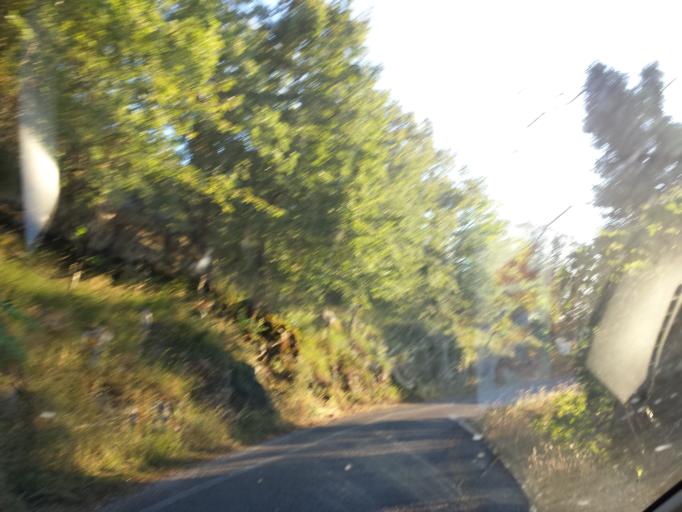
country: GR
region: Ionian Islands
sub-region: Nomos Kerkyras
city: Acharavi
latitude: 39.7482
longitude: 19.8695
